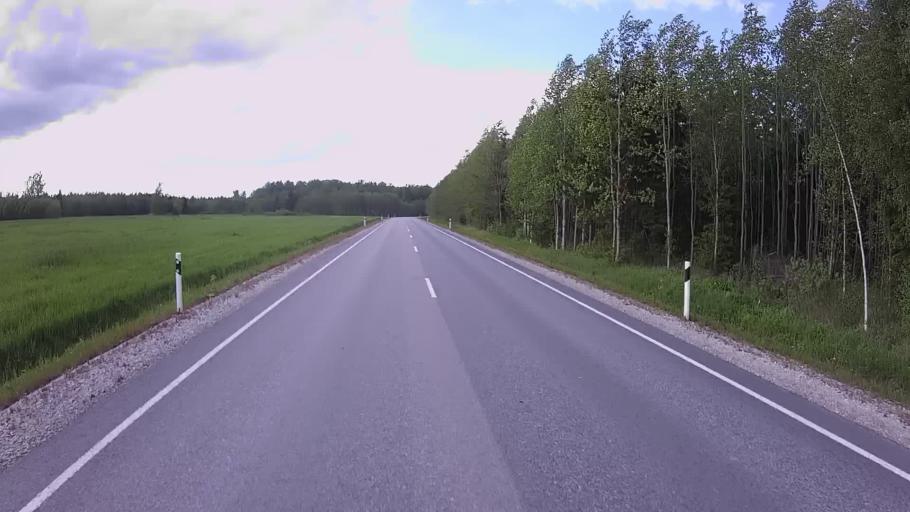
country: EE
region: Jogevamaa
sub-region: Mustvee linn
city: Mustvee
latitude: 58.8778
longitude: 26.8182
